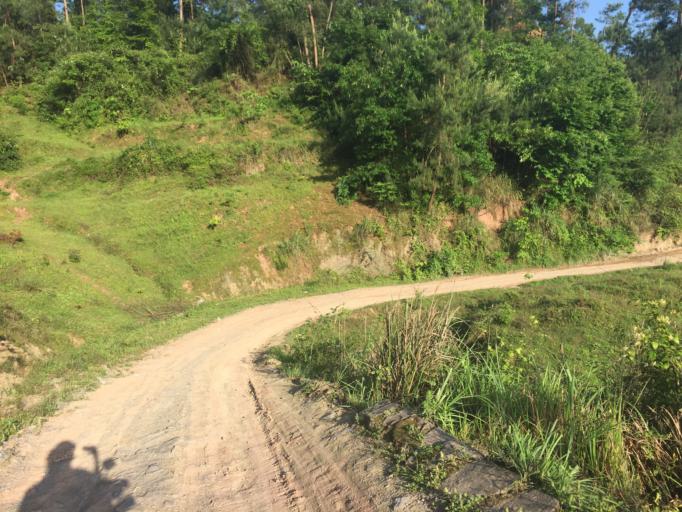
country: CN
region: Guizhou Sheng
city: Xujiaba
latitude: 27.7164
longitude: 108.0250
